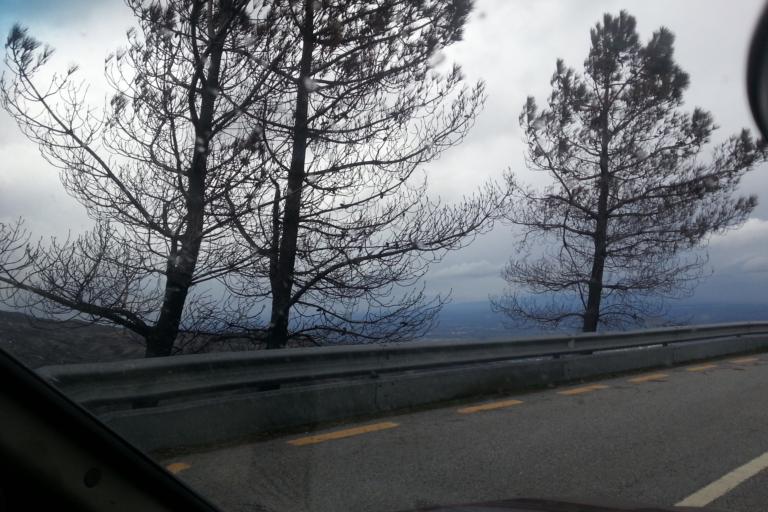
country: PT
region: Guarda
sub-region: Manteigas
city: Manteigas
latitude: 40.4432
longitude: -7.6008
